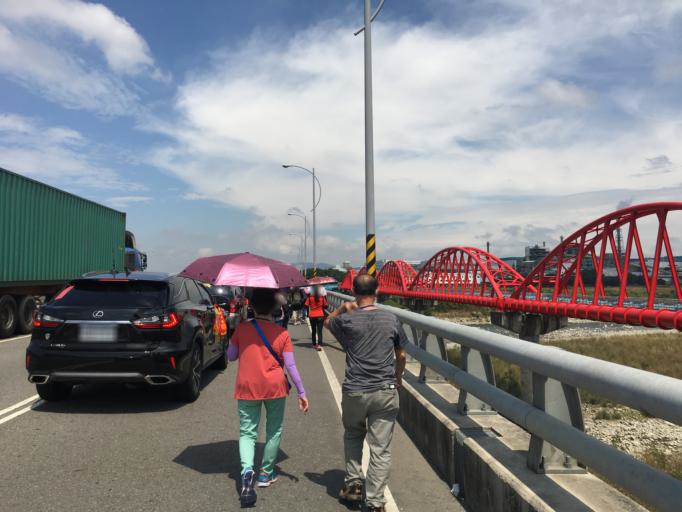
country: TW
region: Taiwan
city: Fengyuan
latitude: 24.2799
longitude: 120.7229
